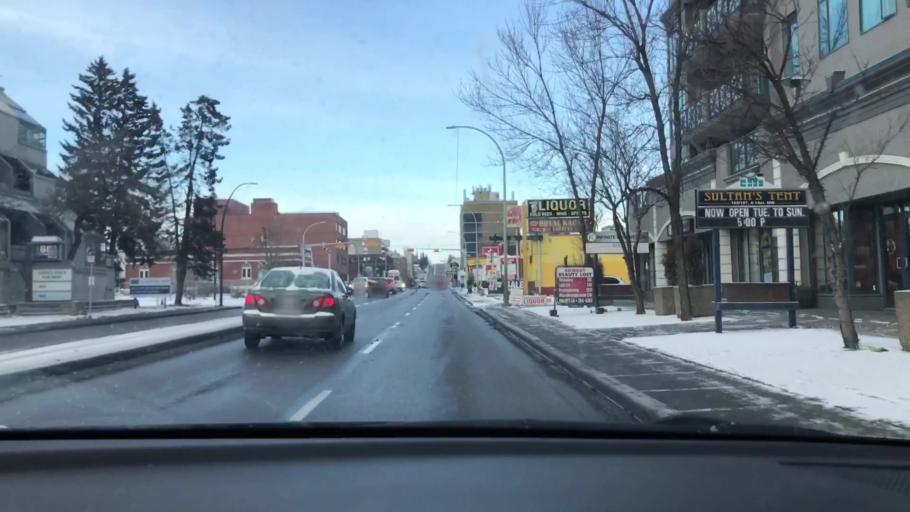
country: CA
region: Alberta
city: Calgary
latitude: 51.0514
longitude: -114.0946
